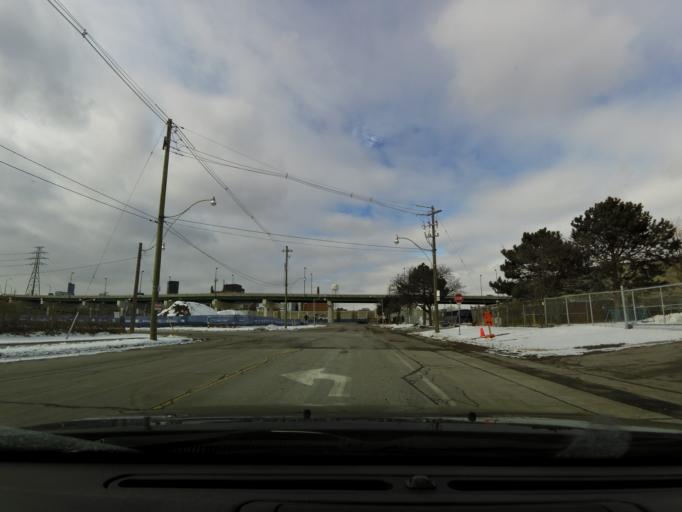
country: CA
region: Ontario
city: Toronto
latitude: 43.6509
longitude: -79.3433
